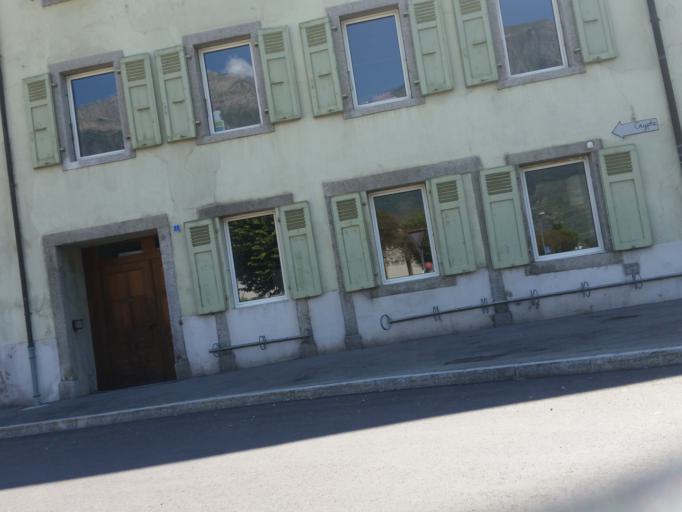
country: CH
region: Valais
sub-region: Martigny District
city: Charrat-les-Chenes
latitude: 46.1212
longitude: 7.1355
